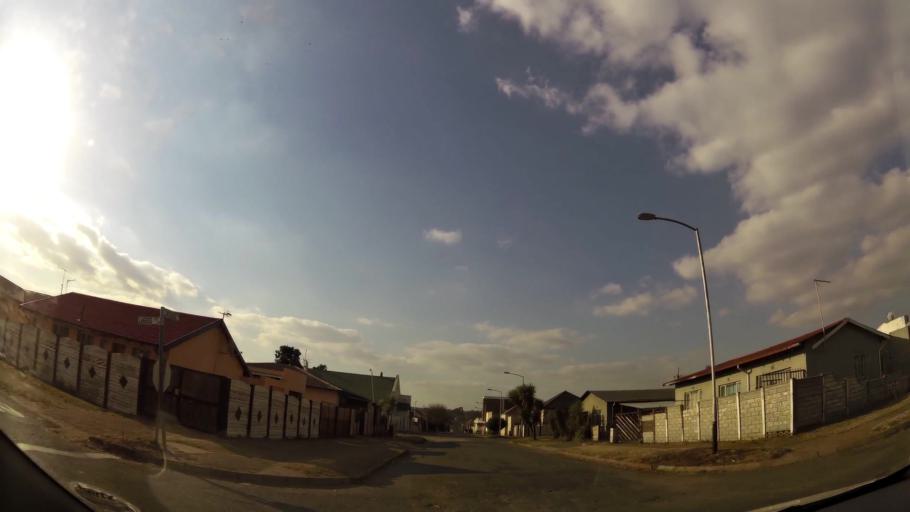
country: ZA
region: Gauteng
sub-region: West Rand District Municipality
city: Krugersdorp
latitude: -26.0989
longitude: 27.7577
